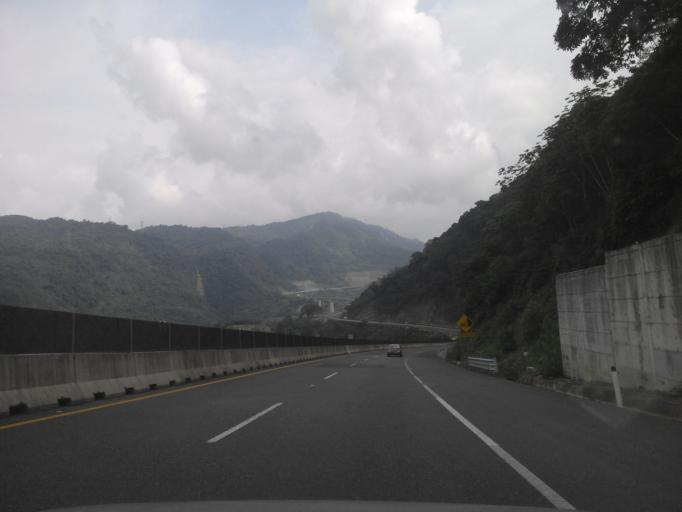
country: MX
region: Puebla
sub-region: Xicotepec
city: San Lorenzo
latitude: 20.3576
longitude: -97.9631
